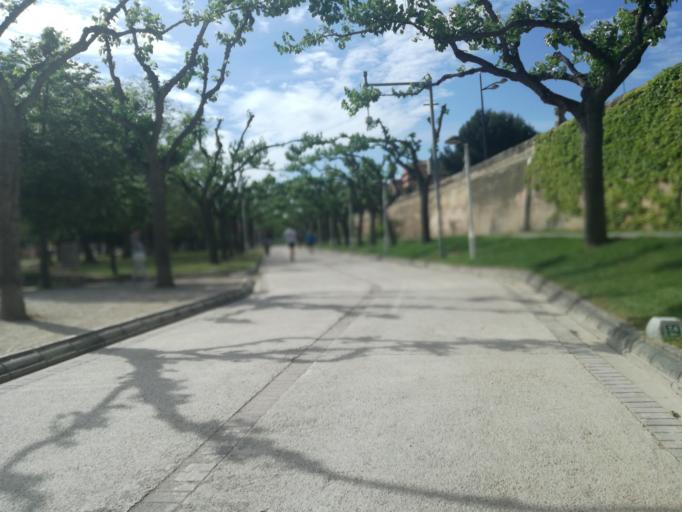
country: ES
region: Valencia
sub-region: Provincia de Valencia
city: Valencia
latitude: 39.4617
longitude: -0.3600
